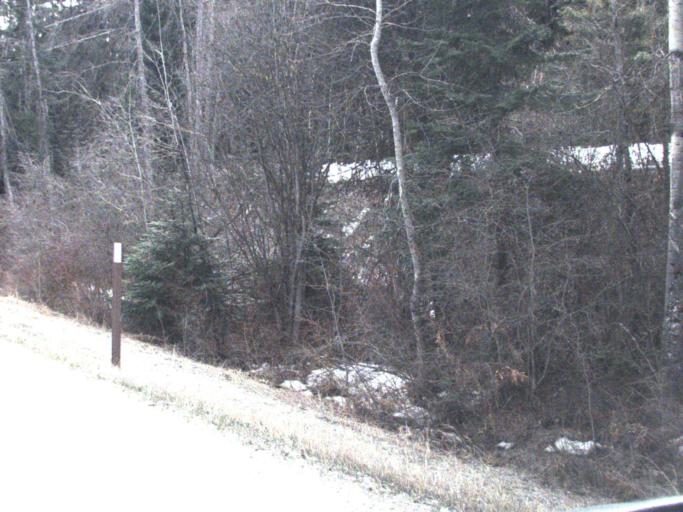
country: US
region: Washington
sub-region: Pend Oreille County
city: Newport
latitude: 48.5209
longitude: -117.2954
